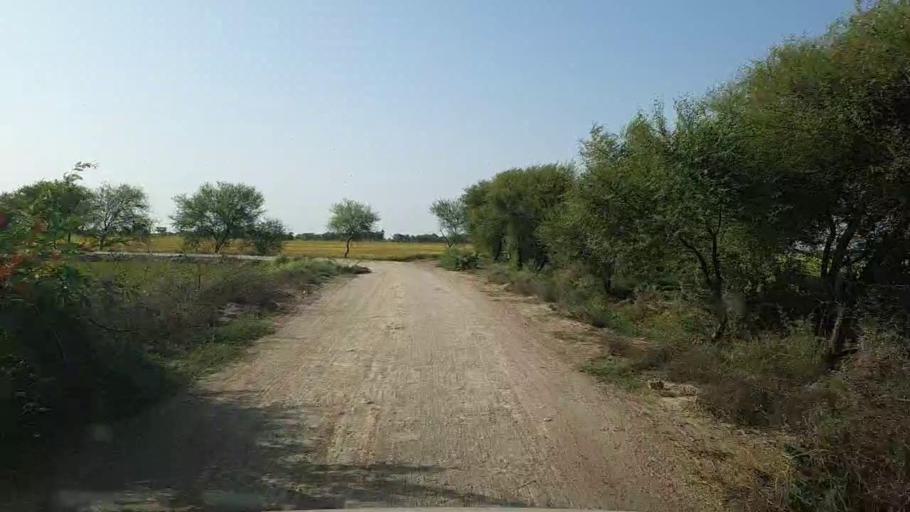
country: PK
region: Sindh
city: Kario
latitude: 24.8227
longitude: 68.4933
